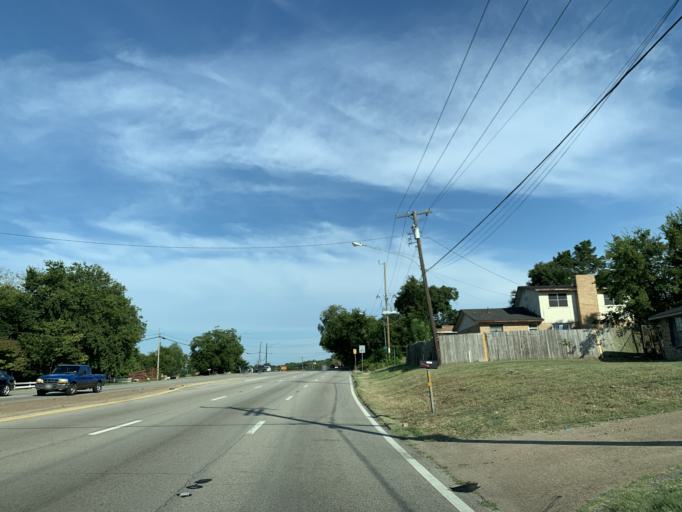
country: US
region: Texas
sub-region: Dallas County
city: Cockrell Hill
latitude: 32.6833
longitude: -96.8093
